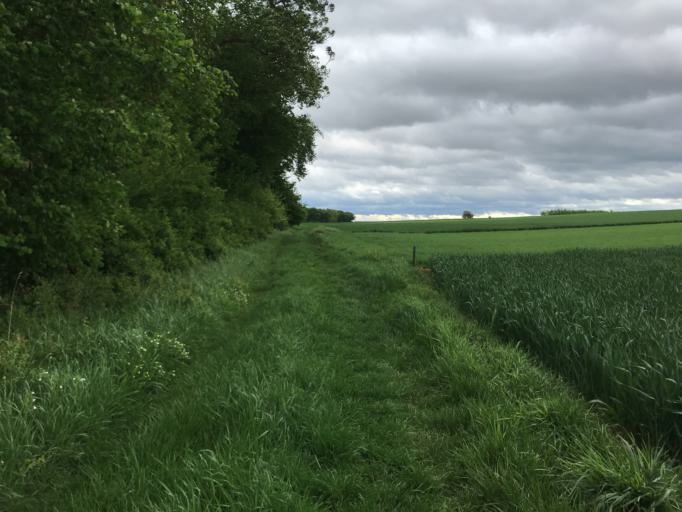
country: DE
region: Rheinland-Pfalz
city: Essenheim
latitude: 49.9524
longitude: 8.1658
